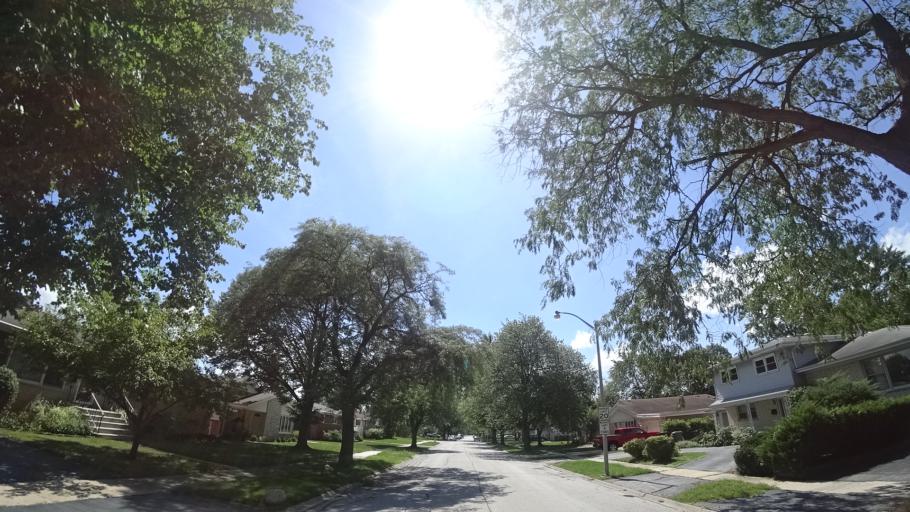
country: US
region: Illinois
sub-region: Cook County
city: Tinley Park
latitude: 41.5721
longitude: -87.7899
